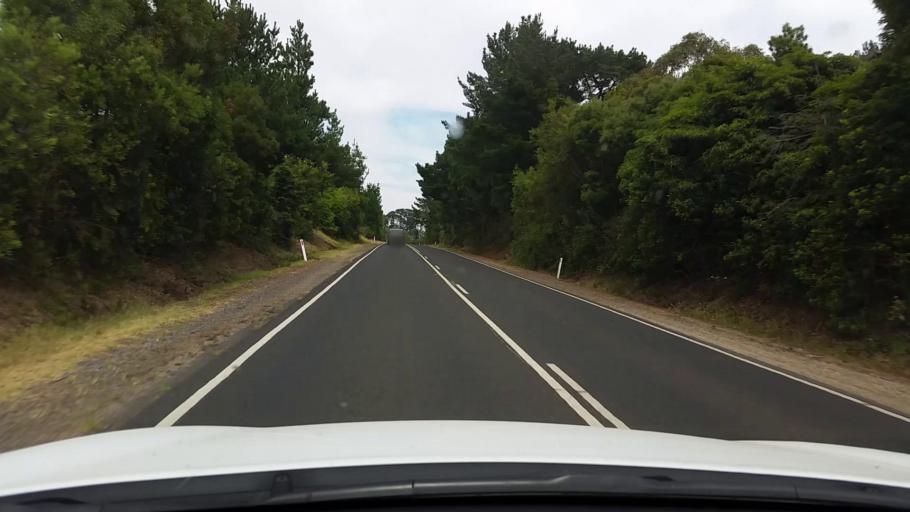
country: AU
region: Victoria
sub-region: Mornington Peninsula
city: Merricks
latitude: -38.4115
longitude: 145.0584
